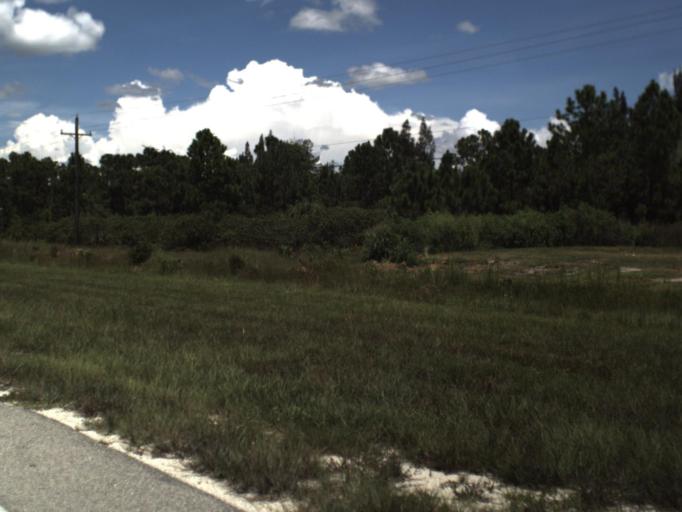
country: US
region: Florida
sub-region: Charlotte County
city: Charlotte Park
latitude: 26.8552
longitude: -81.9858
